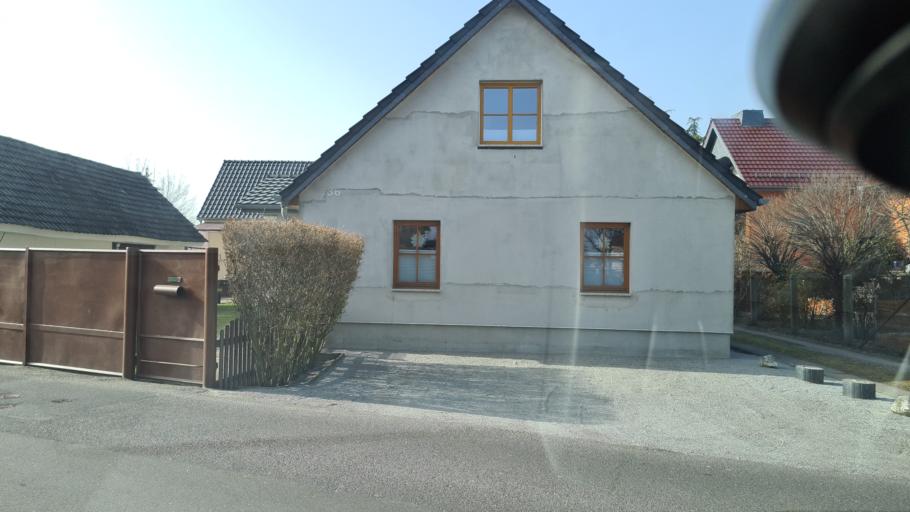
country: DE
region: Brandenburg
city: Cottbus
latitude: 51.7362
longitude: 14.3653
